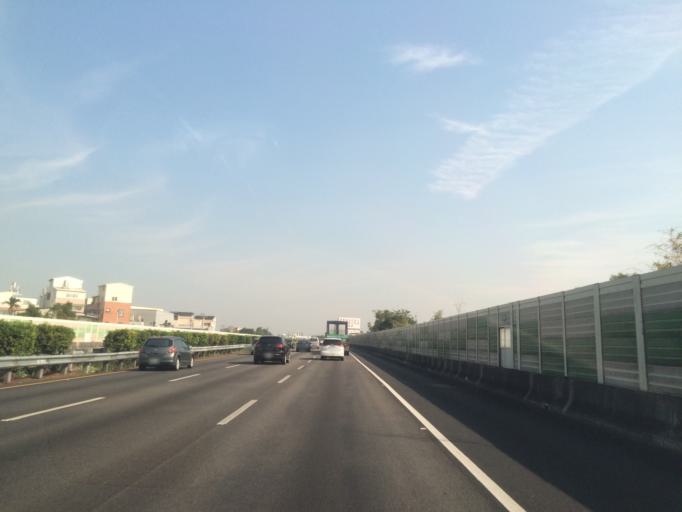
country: TW
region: Taiwan
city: Fengyuan
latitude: 24.2172
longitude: 120.6771
